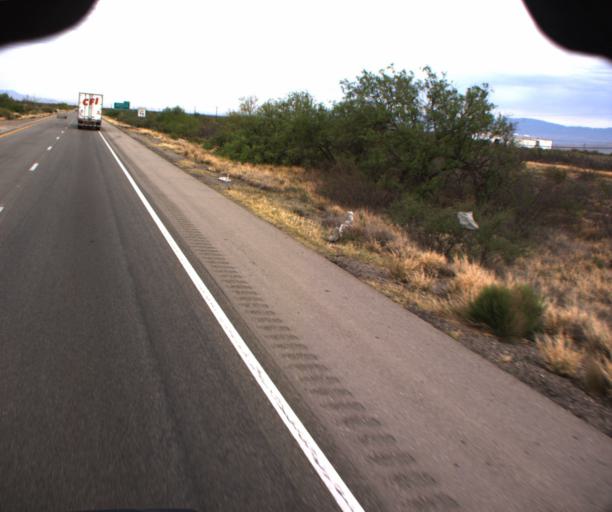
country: US
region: Arizona
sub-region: Pima County
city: Vail
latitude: 32.0150
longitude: -110.7018
